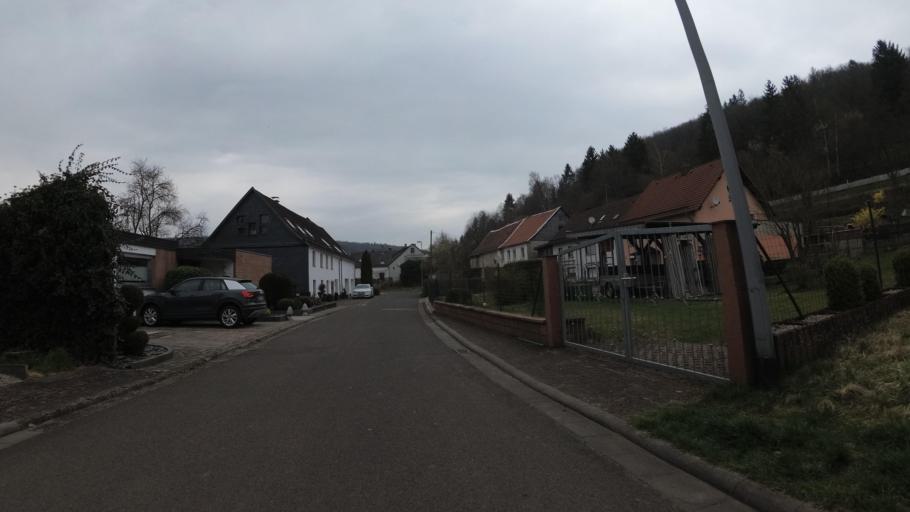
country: DE
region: Rheinland-Pfalz
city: Hoppstadten-Weiersbach
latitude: 49.6189
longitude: 7.1982
